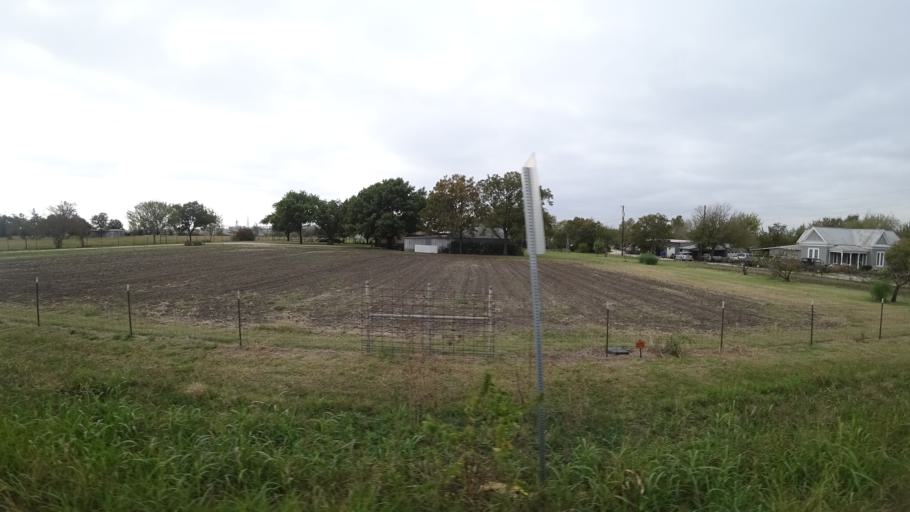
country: US
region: Texas
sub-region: Travis County
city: Pflugerville
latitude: 30.4161
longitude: -97.5743
